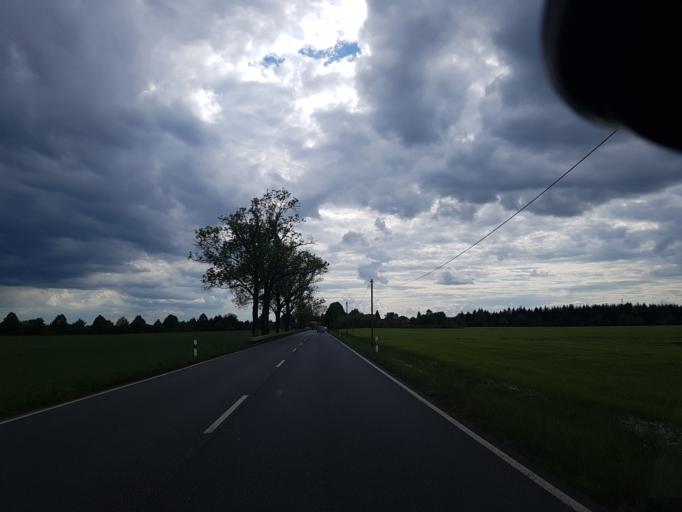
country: DE
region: Brandenburg
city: Neupetershain
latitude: 51.5843
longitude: 14.1009
